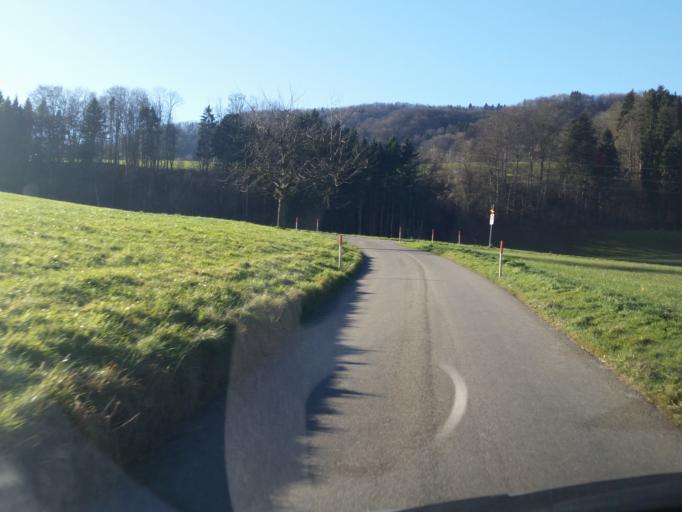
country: CH
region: Aargau
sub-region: Bezirk Bremgarten
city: Rudolfstetten
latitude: 47.3911
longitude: 8.3753
